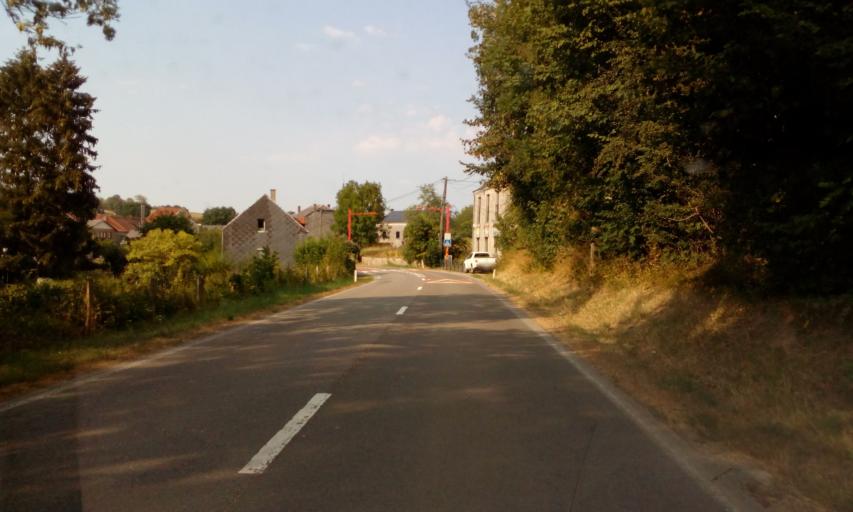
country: BE
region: Wallonia
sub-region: Province du Luxembourg
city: Tellin
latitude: 50.1189
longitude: 5.2477
